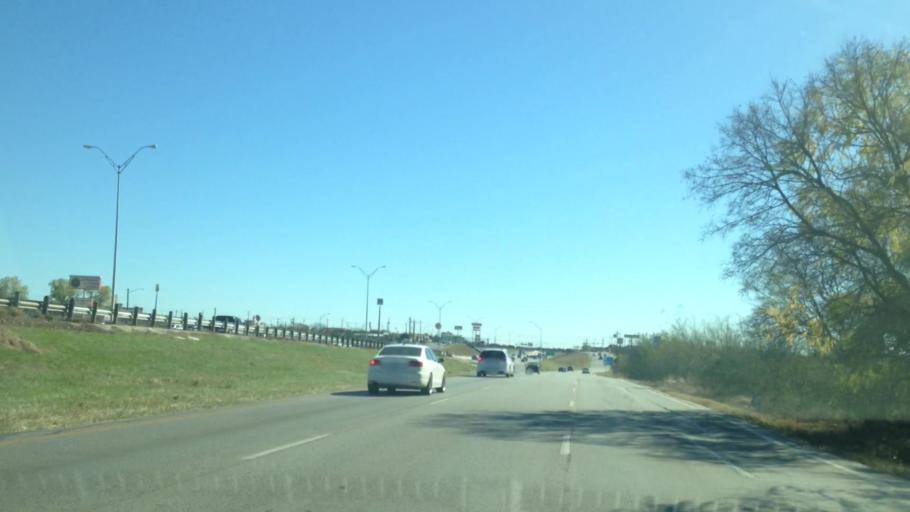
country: US
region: Texas
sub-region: Bexar County
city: Lackland Air Force Base
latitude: 29.3851
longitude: -98.6444
